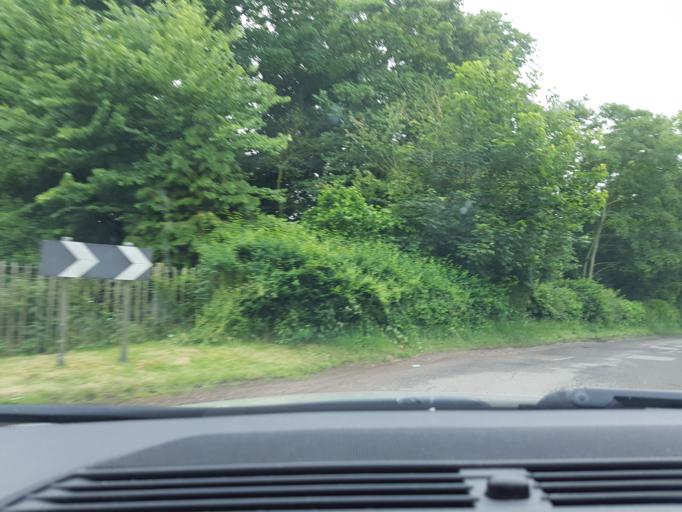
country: GB
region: England
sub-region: Buckinghamshire
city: Steeple Claydon
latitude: 51.9256
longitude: -0.9546
